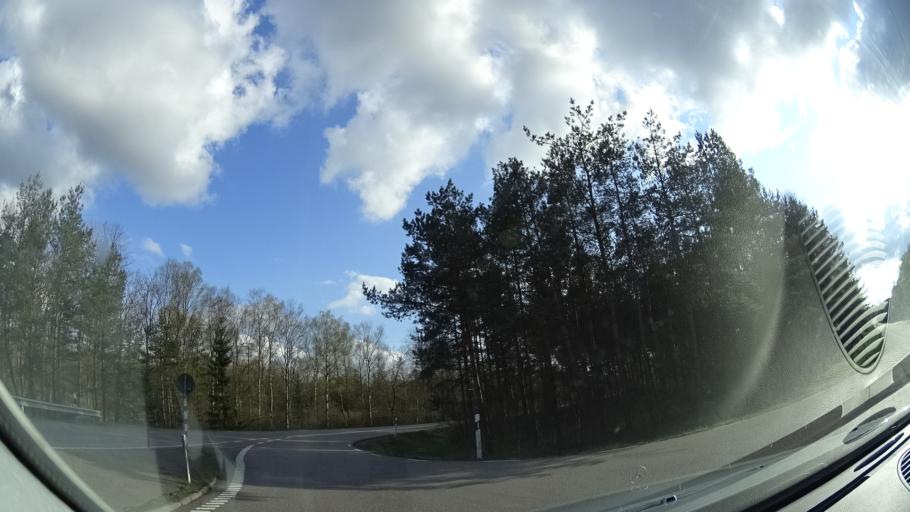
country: SE
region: Skane
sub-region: Perstorps Kommun
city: Perstorp
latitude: 56.1290
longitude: 13.3110
